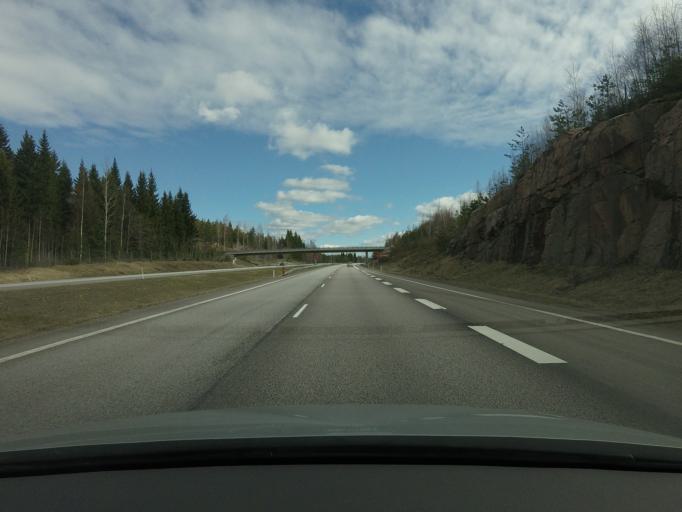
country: FI
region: Uusimaa
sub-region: Porvoo
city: Porvoo
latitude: 60.4543
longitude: 25.8404
